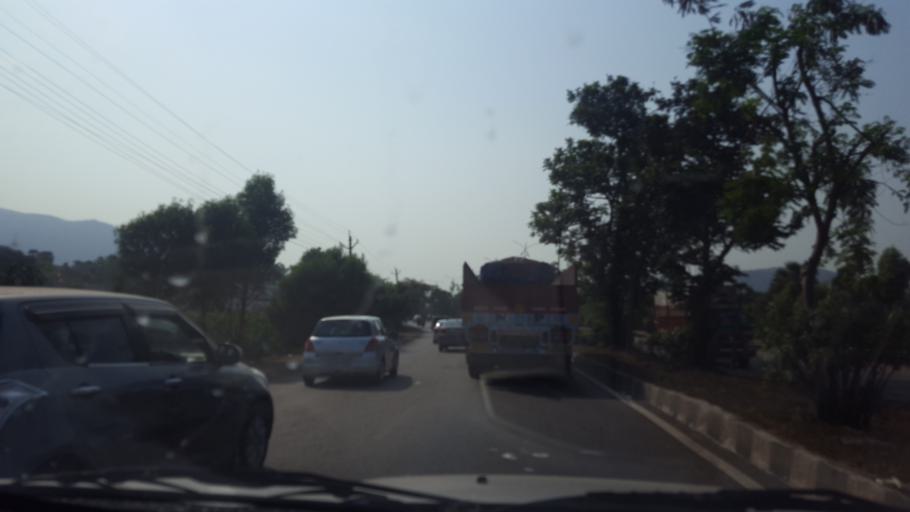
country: IN
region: Andhra Pradesh
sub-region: Vishakhapatnam
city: Anakapalle
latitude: 17.6872
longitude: 83.0897
